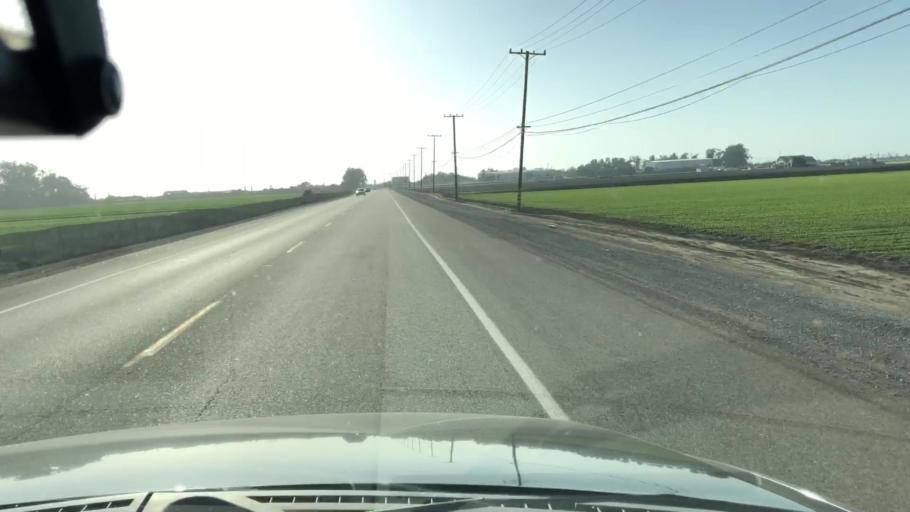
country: US
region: California
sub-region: Ventura County
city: Oxnard Shores
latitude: 34.2196
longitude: -119.2402
